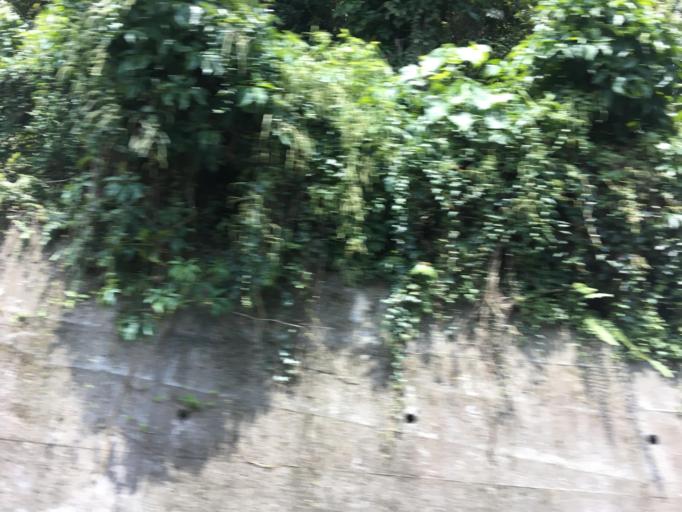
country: TW
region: Taiwan
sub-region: Yilan
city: Yilan
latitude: 24.8182
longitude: 121.7347
